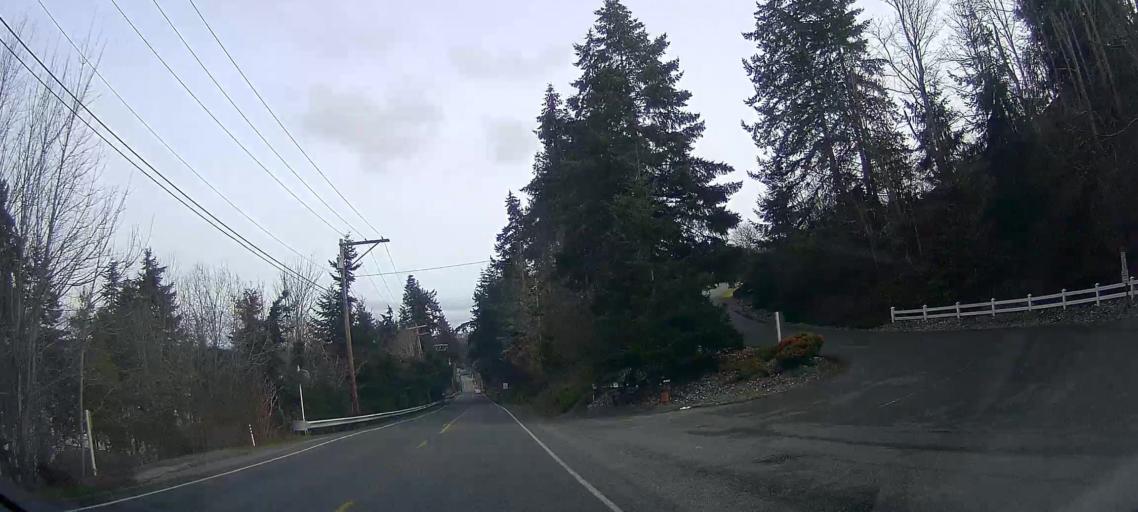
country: US
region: Washington
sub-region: Island County
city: Camano
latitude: 48.2506
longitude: -122.4919
